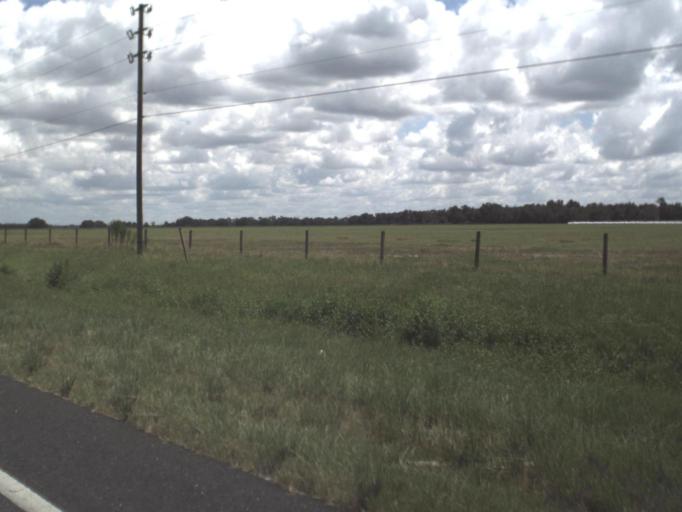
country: US
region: Florida
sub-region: Polk County
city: Wahneta
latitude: 27.9161
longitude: -81.7169
